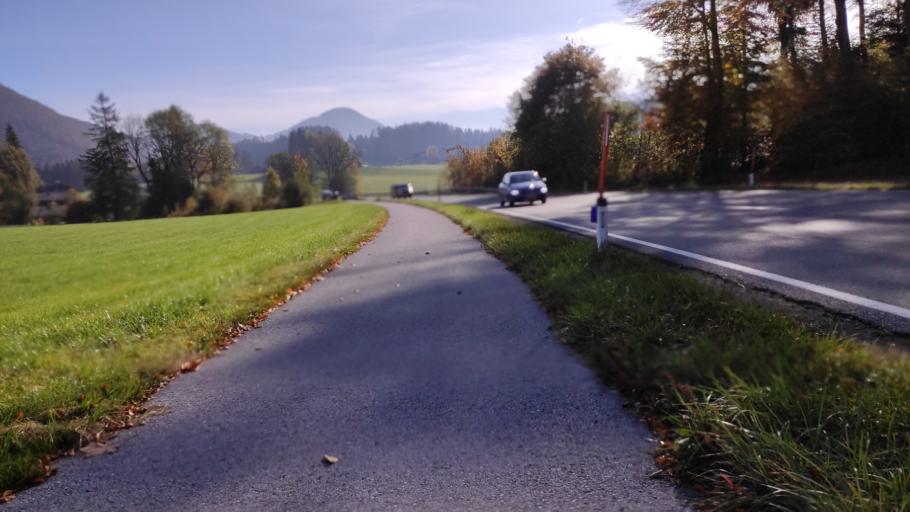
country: AT
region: Salzburg
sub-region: Politischer Bezirk Salzburg-Umgebung
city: Koppl
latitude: 47.8143
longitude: 13.1688
